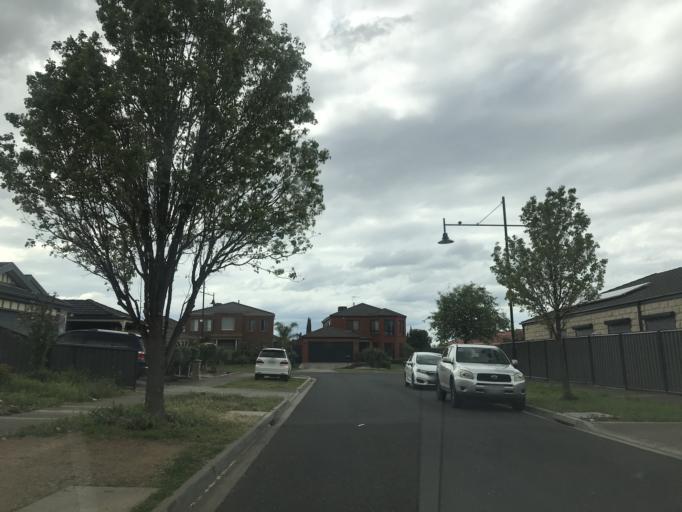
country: AU
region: Victoria
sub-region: Brimbank
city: Derrimut
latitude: -37.7956
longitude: 144.7664
